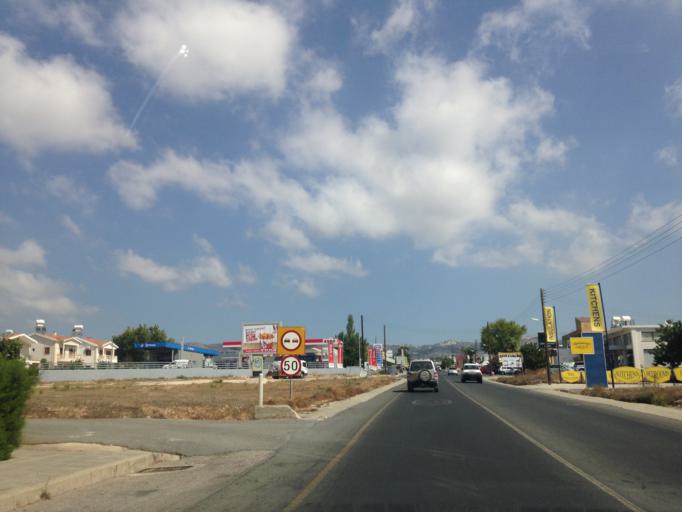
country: CY
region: Pafos
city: Empa
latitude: 34.7985
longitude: 32.4407
